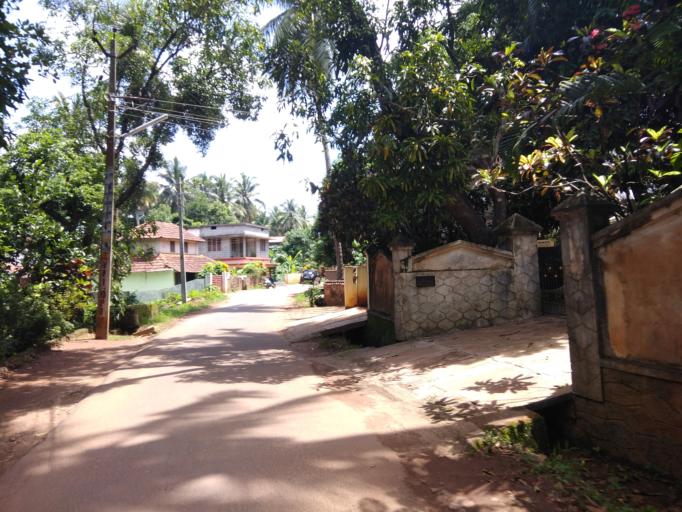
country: IN
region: Kerala
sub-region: Thrissur District
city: Trichur
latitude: 10.5449
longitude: 76.1750
